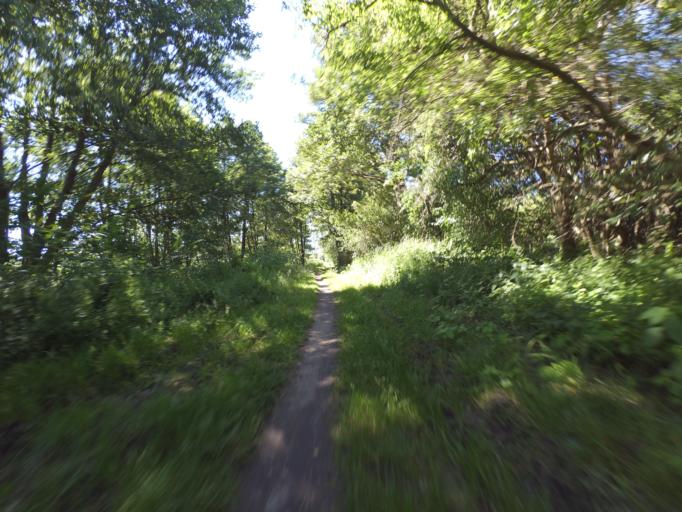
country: DE
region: Mecklenburg-Vorpommern
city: Plau am See
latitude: 53.5024
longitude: 12.3322
